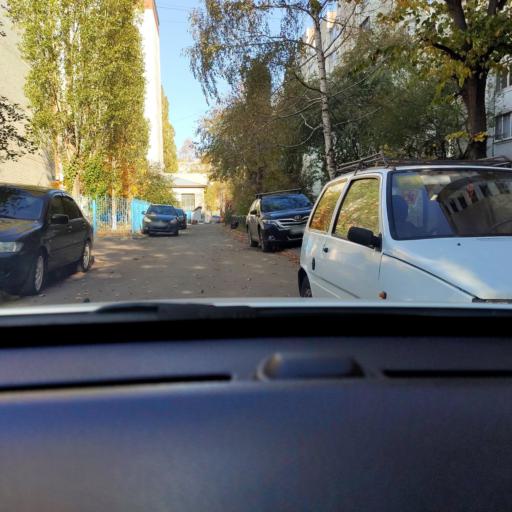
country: RU
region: Voronezj
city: Podgornoye
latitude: 51.7094
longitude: 39.1715
